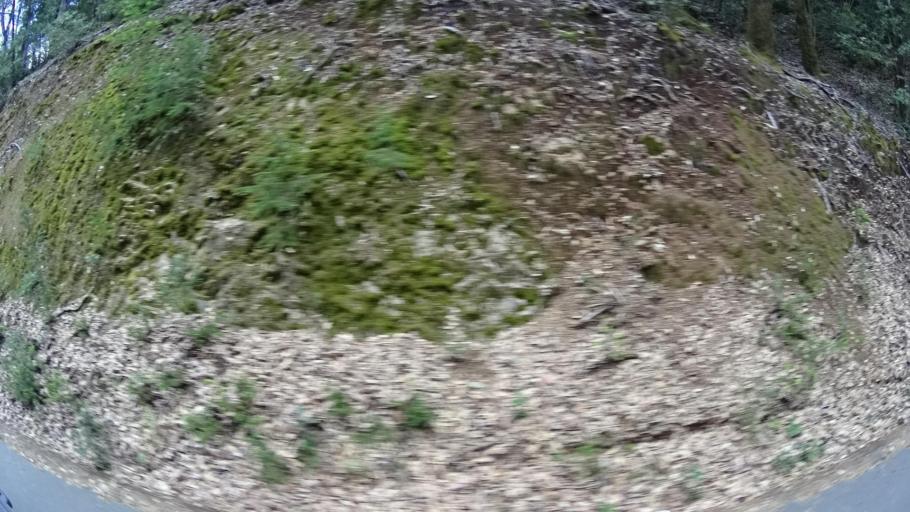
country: US
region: California
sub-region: Humboldt County
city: Redway
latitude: 40.0161
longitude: -123.9937
